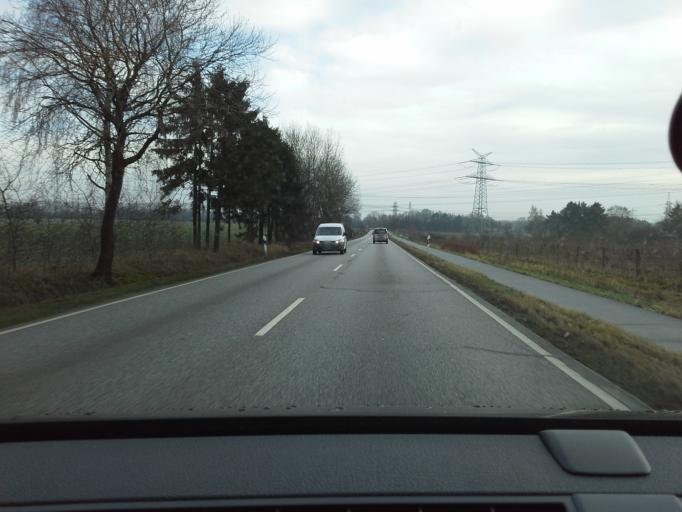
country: DE
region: Schleswig-Holstein
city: Ellerau
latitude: 53.7402
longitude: 9.9603
